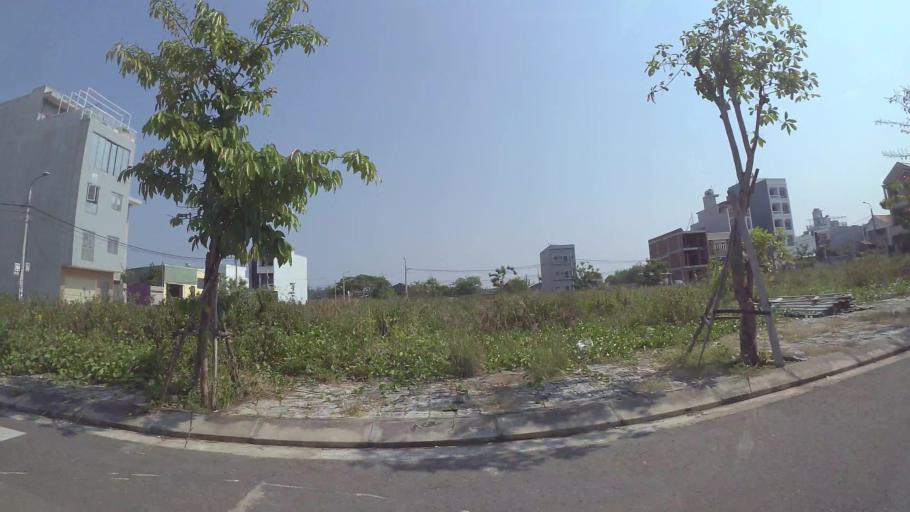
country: VN
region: Da Nang
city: Ngu Hanh Son
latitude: 16.0373
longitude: 108.2459
